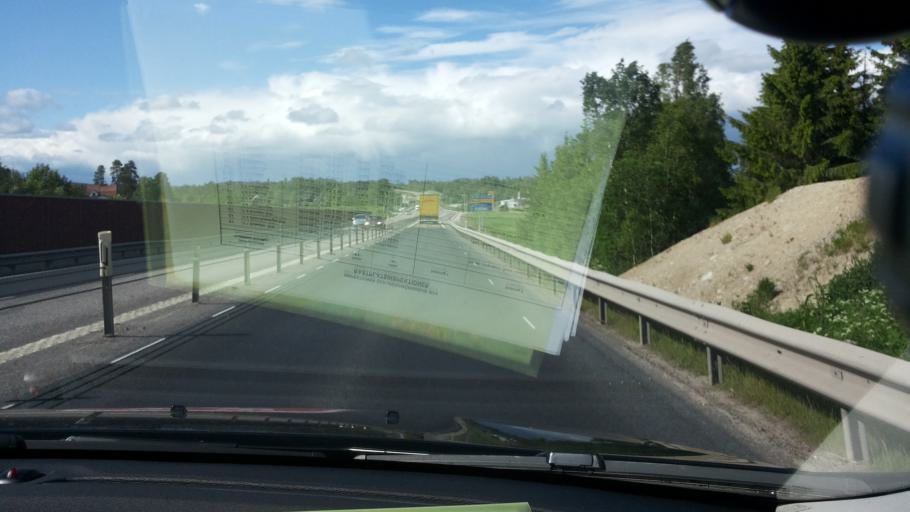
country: SE
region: Vaesternorrland
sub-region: Sundsvalls Kommun
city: Njurundabommen
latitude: 62.2431
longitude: 17.3738
